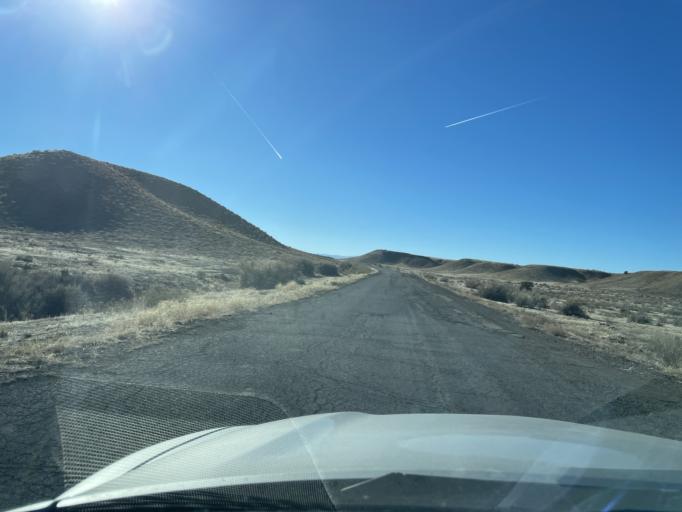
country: US
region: Colorado
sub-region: Mesa County
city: Loma
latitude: 39.2057
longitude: -109.1070
